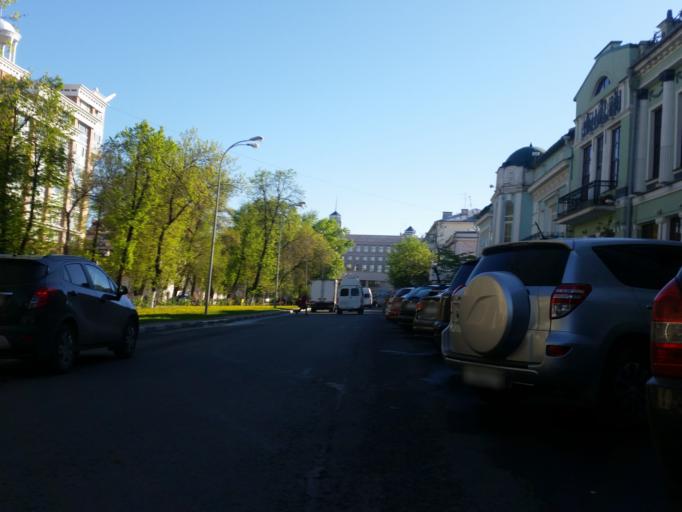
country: RU
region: Ulyanovsk
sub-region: Ulyanovskiy Rayon
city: Ulyanovsk
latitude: 54.3202
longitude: 48.4001
